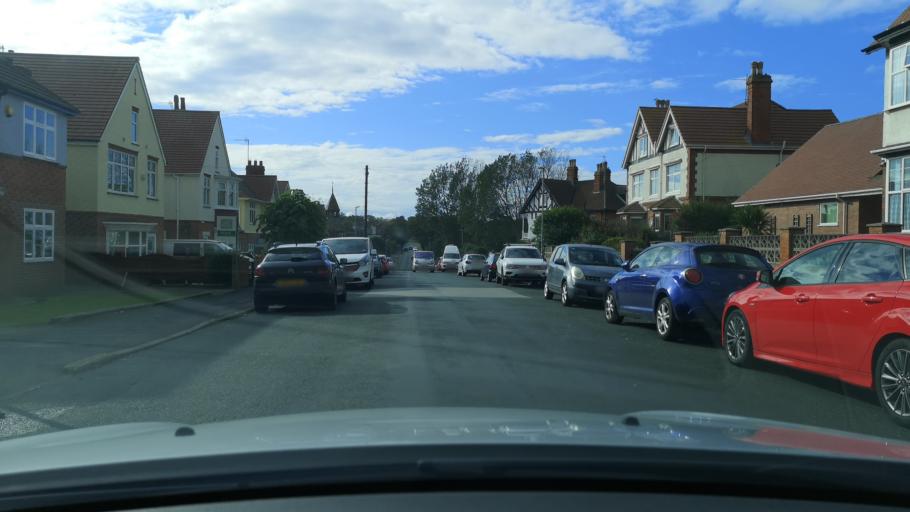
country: GB
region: England
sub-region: East Riding of Yorkshire
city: Hornsea
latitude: 53.9155
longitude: -0.1633
